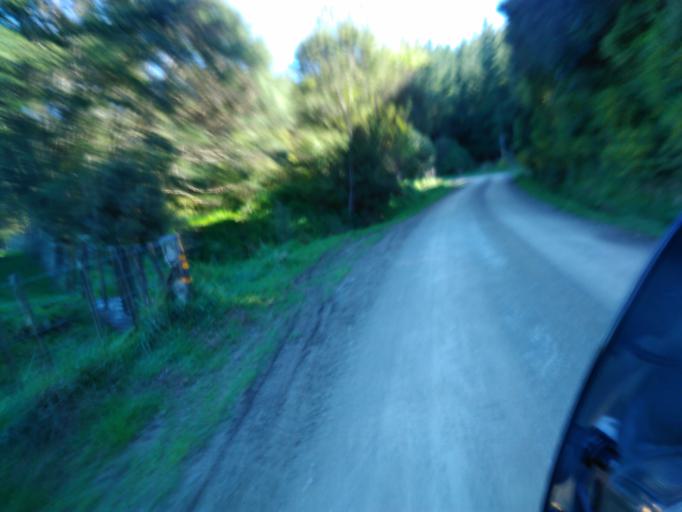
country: NZ
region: Gisborne
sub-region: Gisborne District
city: Gisborne
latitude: -38.3997
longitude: 177.6801
